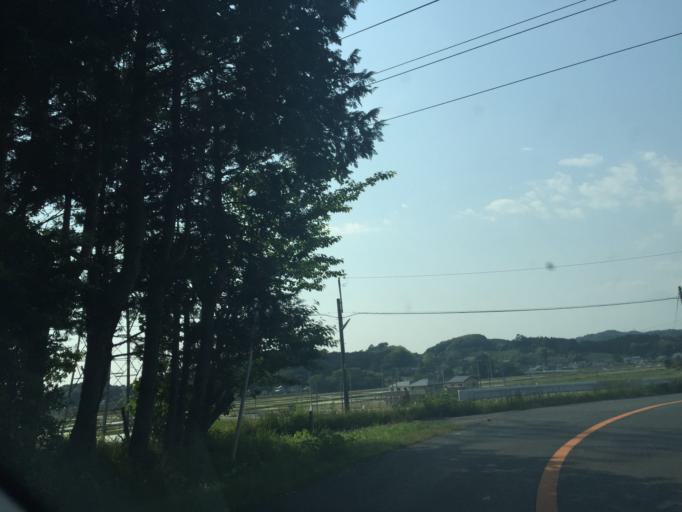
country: JP
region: Shizuoka
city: Kakegawa
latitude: 34.7925
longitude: 137.9928
